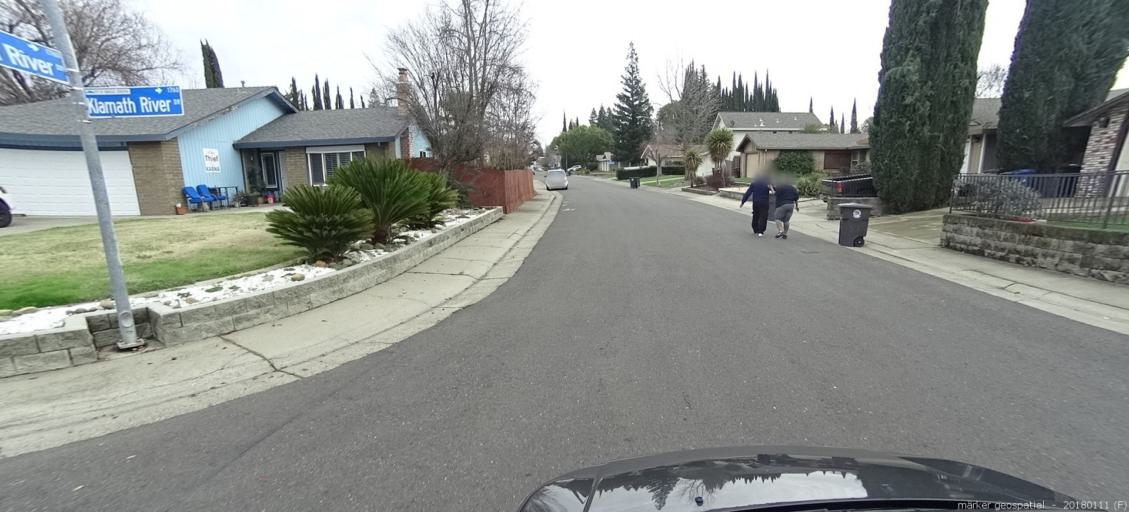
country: US
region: California
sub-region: Sacramento County
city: Fair Oaks
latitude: 38.6207
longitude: -121.2786
